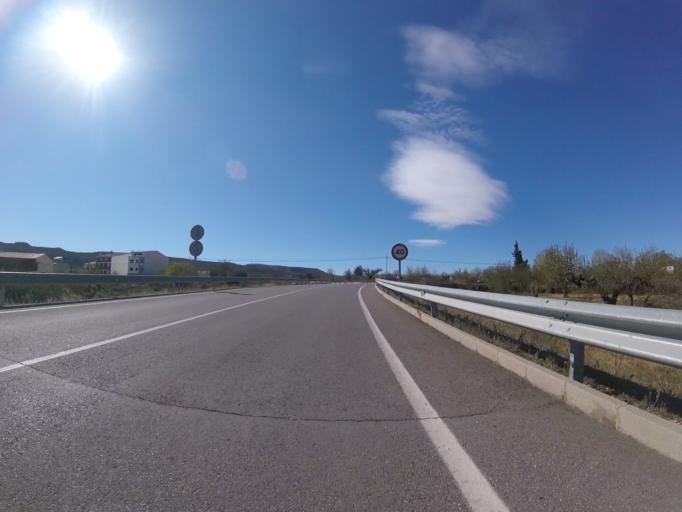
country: ES
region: Valencia
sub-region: Provincia de Castello
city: Albocasser
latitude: 40.3588
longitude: 0.0187
